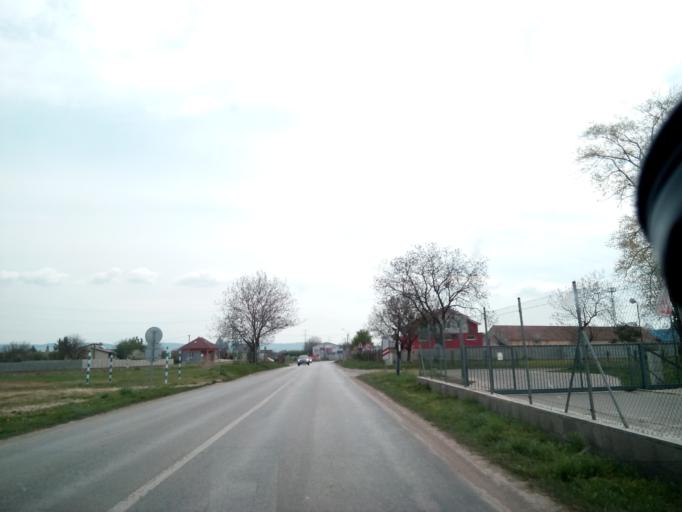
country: SK
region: Trnavsky
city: Vrbove
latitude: 48.6105
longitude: 17.7429
